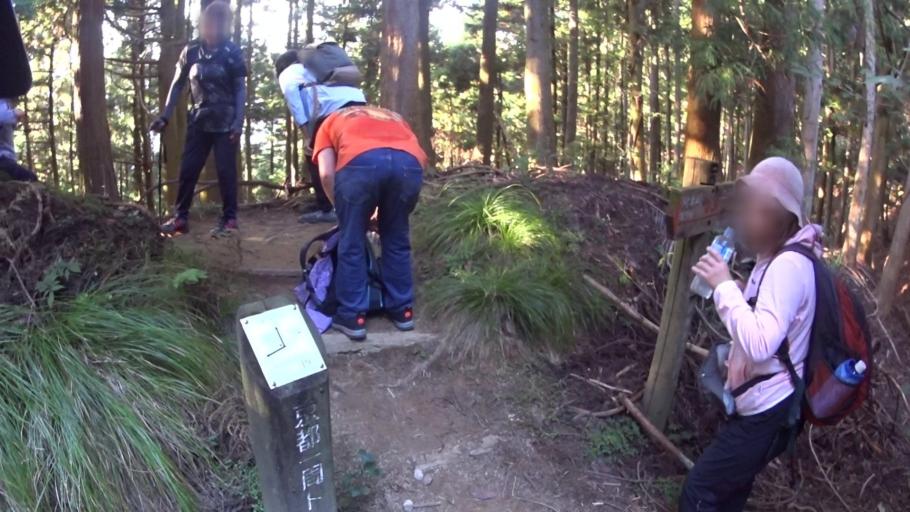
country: JP
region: Shiga Prefecture
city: Kitahama
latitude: 35.1083
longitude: 135.8405
